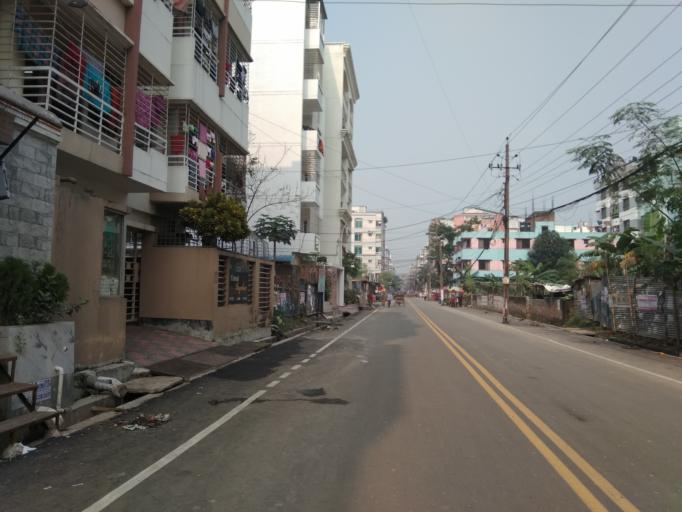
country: BD
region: Dhaka
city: Tungi
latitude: 23.8681
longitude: 90.3833
